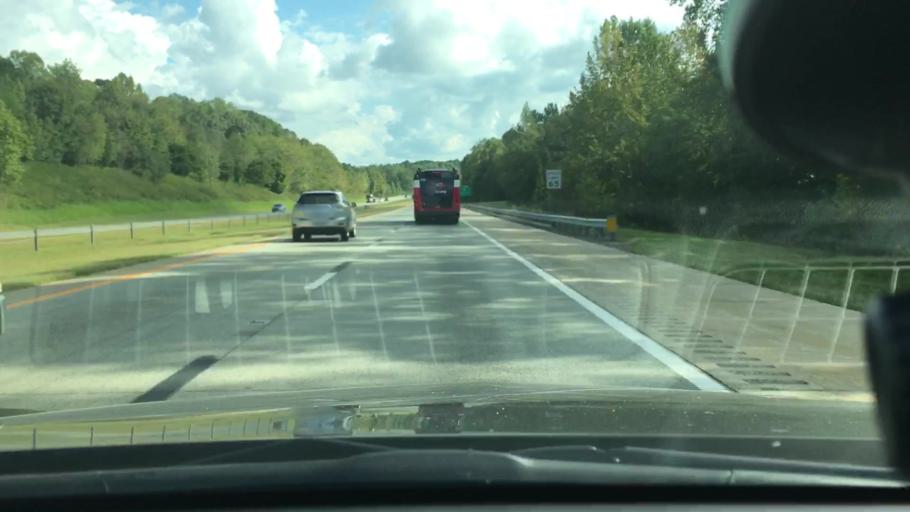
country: US
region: North Carolina
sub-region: Orange County
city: Hillsborough
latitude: 36.0010
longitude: -79.0789
